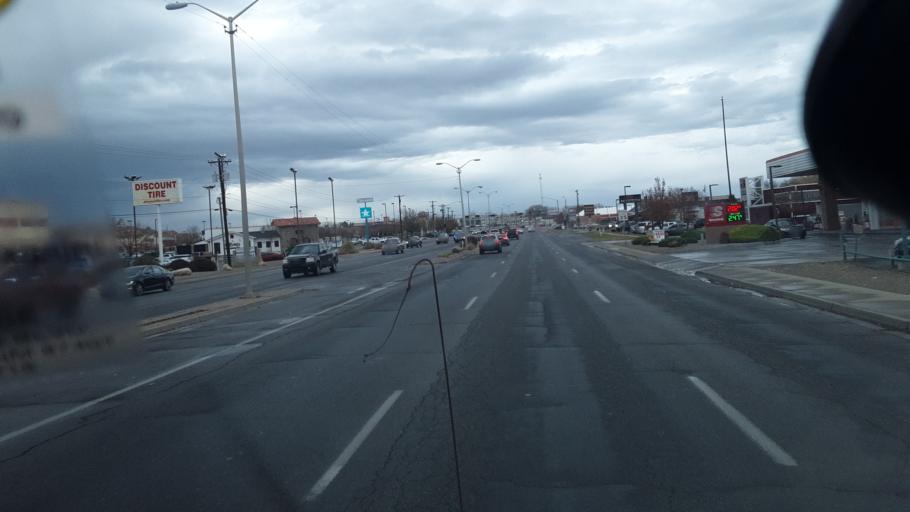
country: US
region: New Mexico
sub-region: San Juan County
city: Farmington
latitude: 36.7483
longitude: -108.1612
